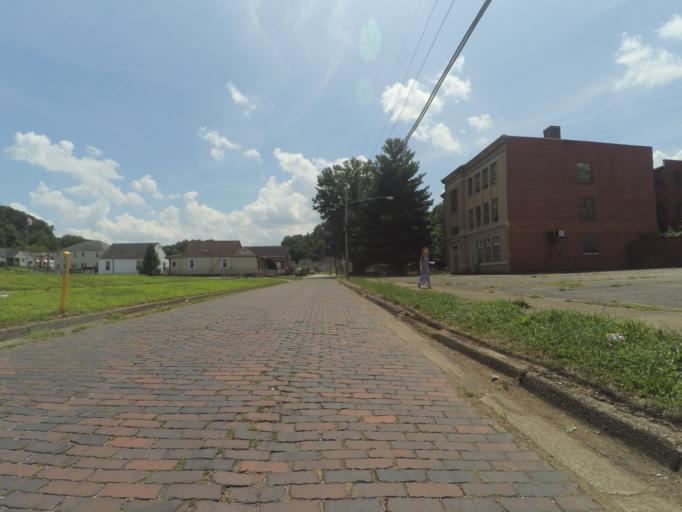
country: US
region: West Virginia
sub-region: Cabell County
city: Huntington
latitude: 38.4181
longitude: -82.4122
